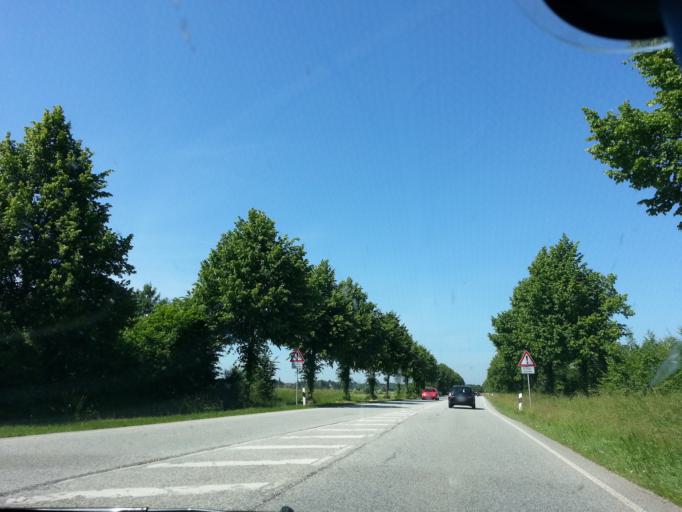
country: DE
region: Schleswig-Holstein
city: Harmsdorf
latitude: 53.6886
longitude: 10.7294
